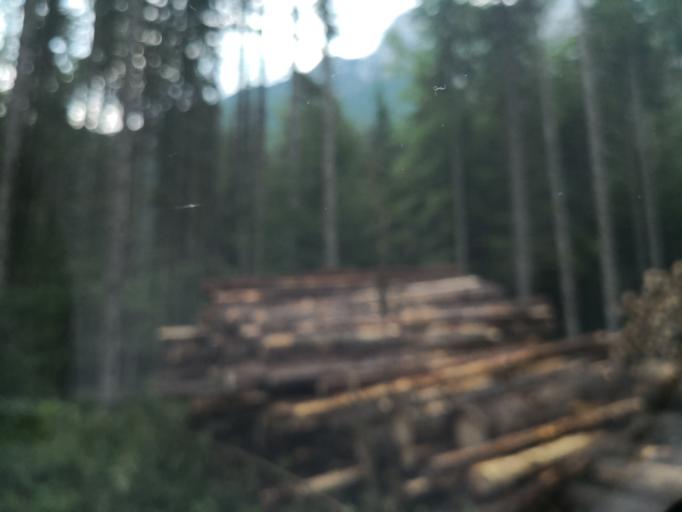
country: SI
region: Jezersko
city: Zgornje Jezersko
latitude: 46.3851
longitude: 14.5366
